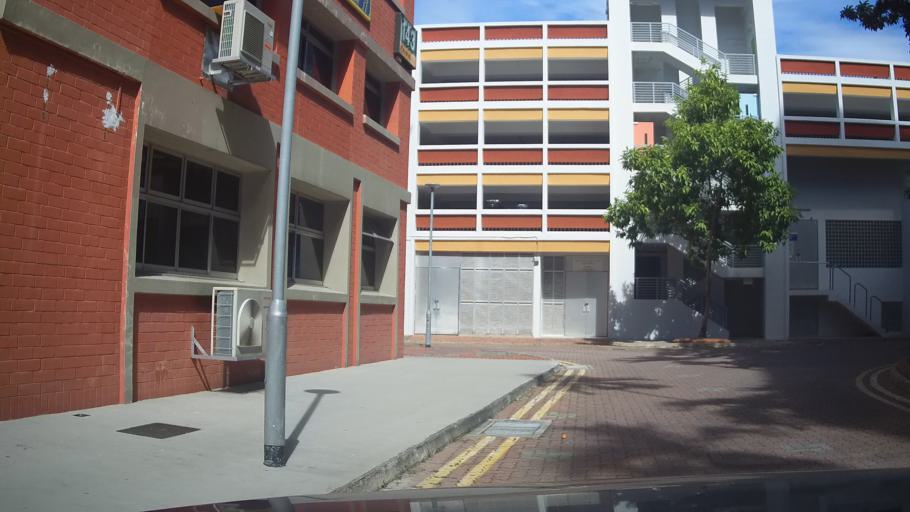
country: SG
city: Singapore
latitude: 1.3625
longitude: 103.9603
